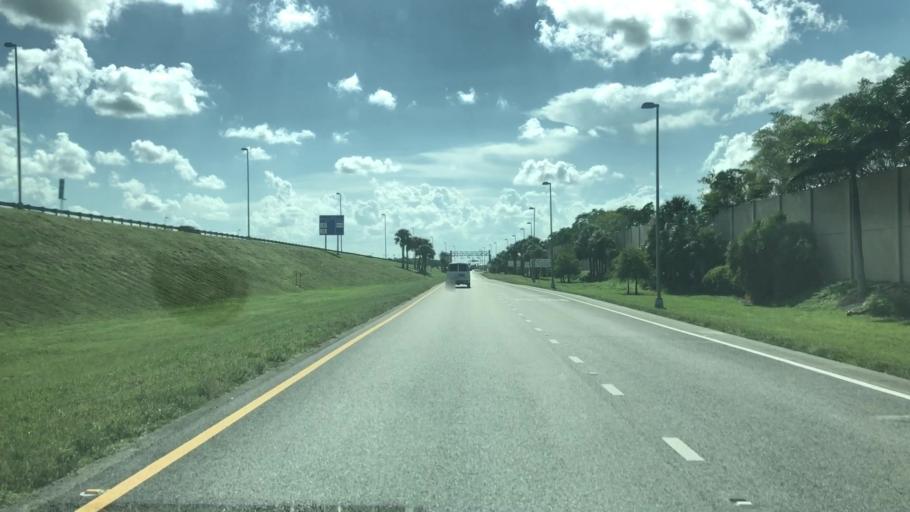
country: US
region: Florida
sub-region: Broward County
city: Parkland
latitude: 26.3025
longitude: -80.2514
